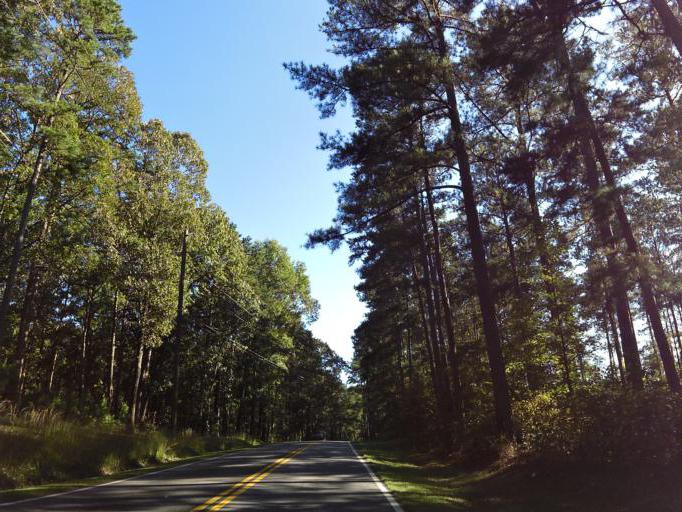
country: US
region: Georgia
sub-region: Bartow County
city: Emerson
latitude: 34.1431
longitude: -84.6989
